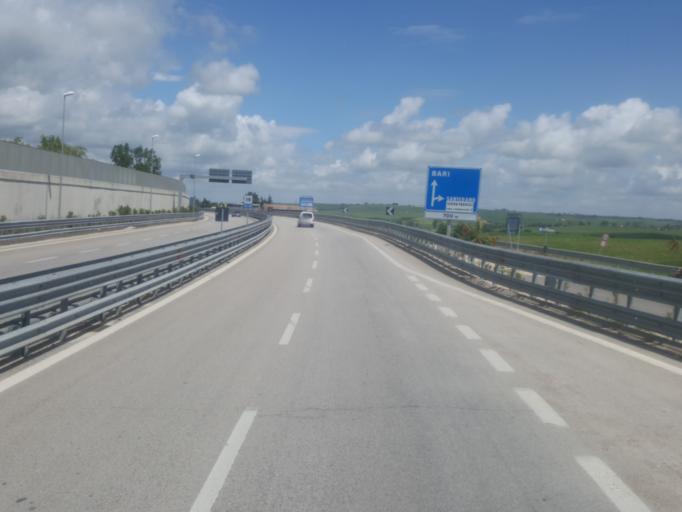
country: IT
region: Basilicate
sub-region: Provincia di Matera
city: Matera
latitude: 40.6922
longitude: 16.5915
